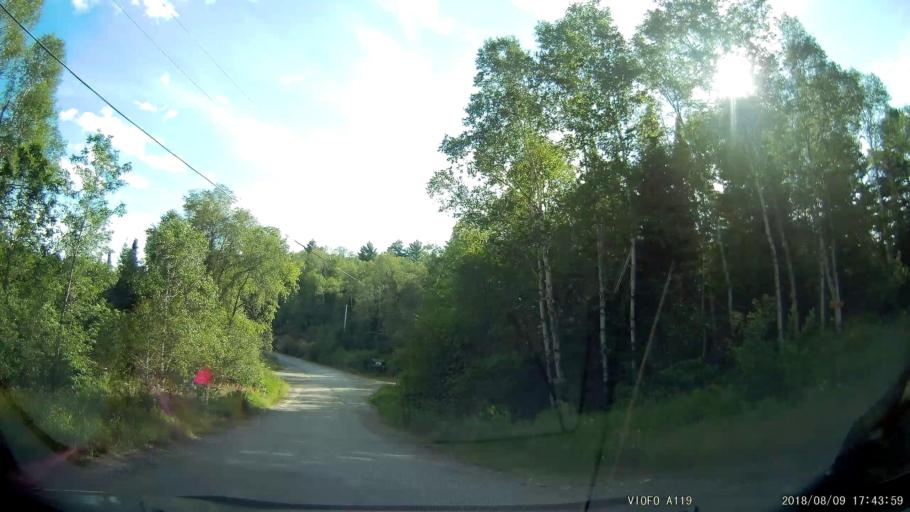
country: CA
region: Ontario
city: Rayside-Balfour
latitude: 46.6089
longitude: -81.5327
